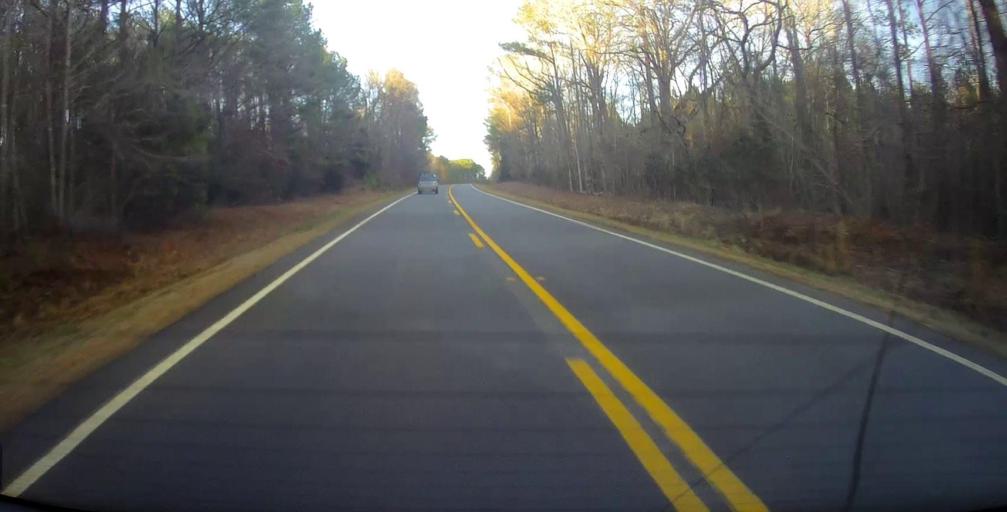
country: US
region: Georgia
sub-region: Talbot County
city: Sardis
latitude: 32.7115
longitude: -84.6872
